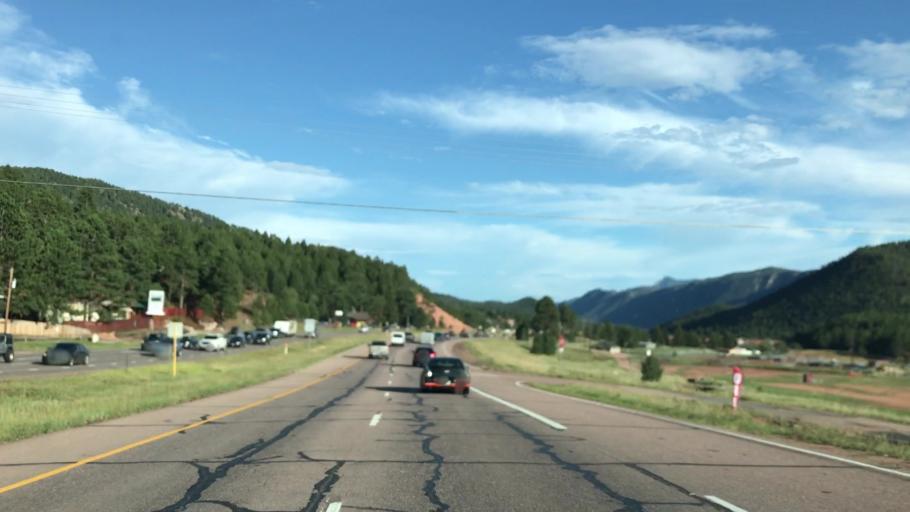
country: US
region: Colorado
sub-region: Teller County
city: Woodland Park
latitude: 38.9808
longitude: -105.0439
